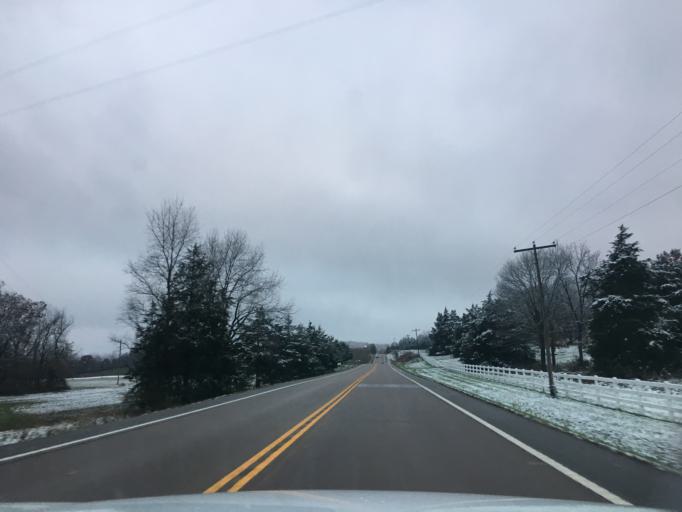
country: US
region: Missouri
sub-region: Osage County
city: Linn
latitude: 38.4691
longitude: -91.7639
